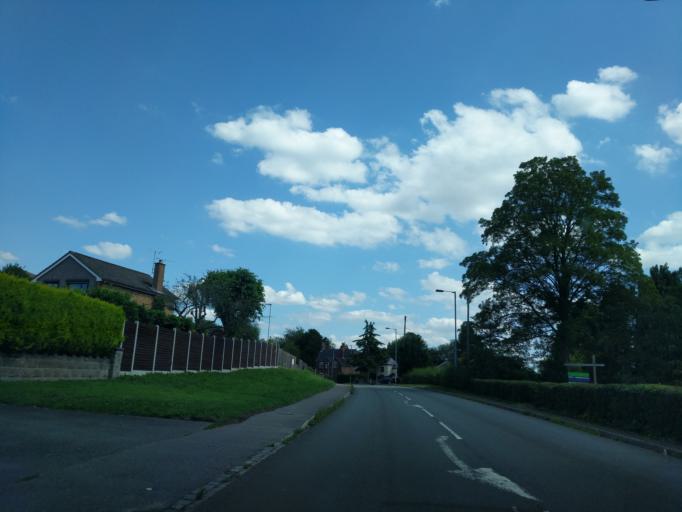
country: GB
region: England
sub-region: Staffordshire
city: Cheadle
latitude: 52.9440
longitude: -1.9751
